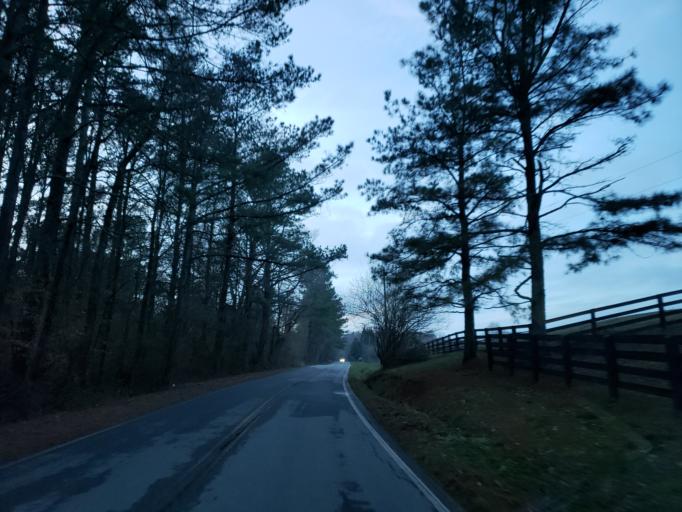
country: US
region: Georgia
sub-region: Cherokee County
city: Ball Ground
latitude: 34.2498
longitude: -84.3359
